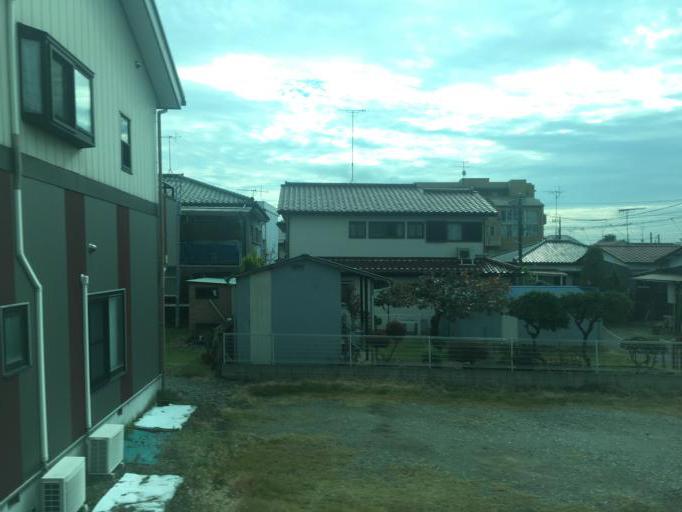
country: JP
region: Tokyo
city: Hino
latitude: 35.6848
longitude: 139.4338
